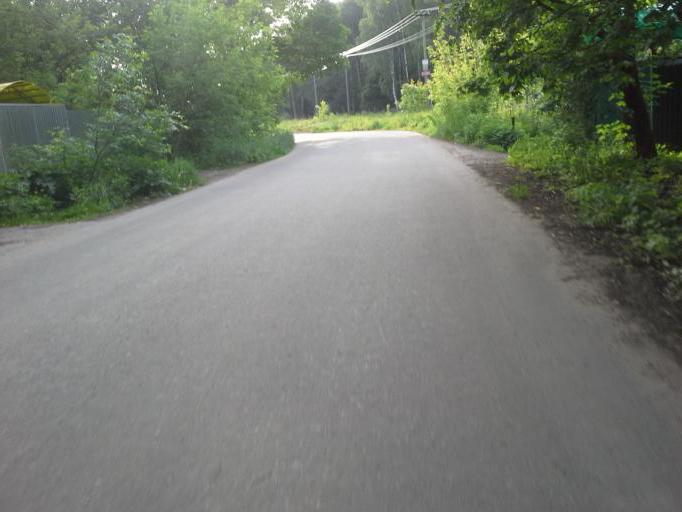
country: RU
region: Moskovskaya
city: Kokoshkino
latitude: 55.6096
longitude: 37.1814
